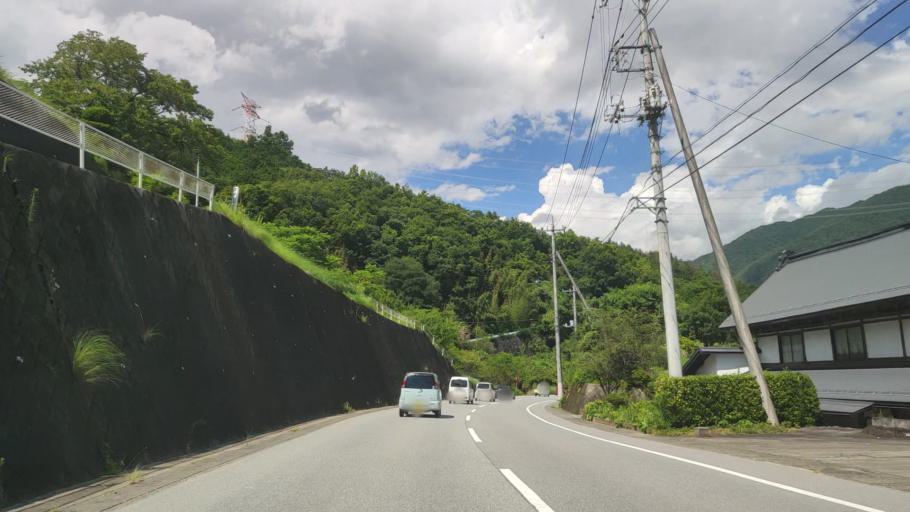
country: JP
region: Yamanashi
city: Enzan
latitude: 35.7575
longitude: 138.7272
